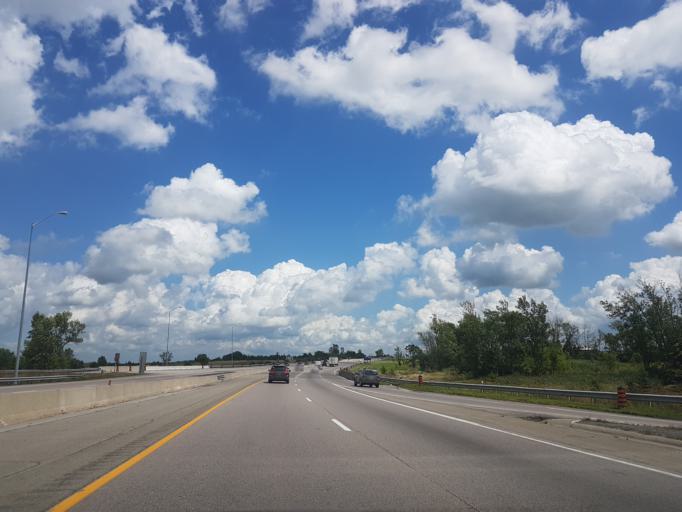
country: CA
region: Ontario
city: Greater Napanee
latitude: 44.2656
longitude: -76.9625
